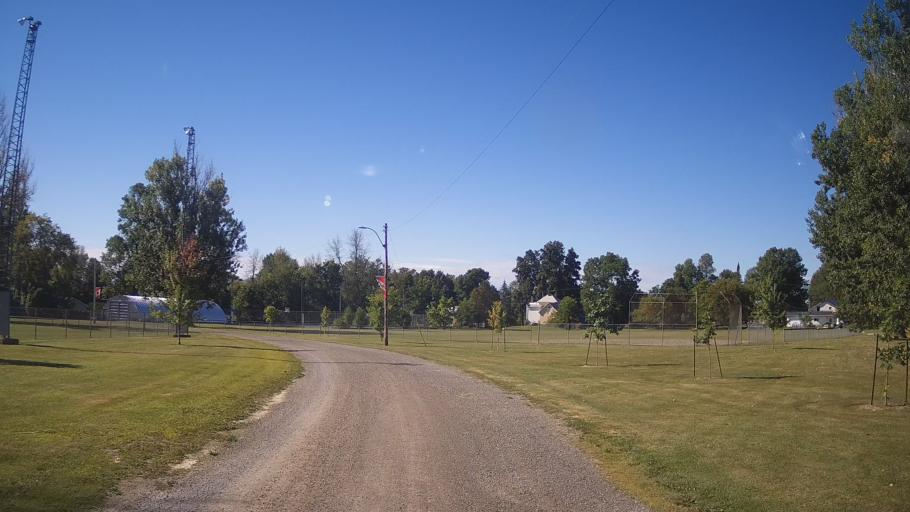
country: CA
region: Ontario
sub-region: Lanark County
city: Smiths Falls
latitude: 44.8406
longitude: -75.8857
